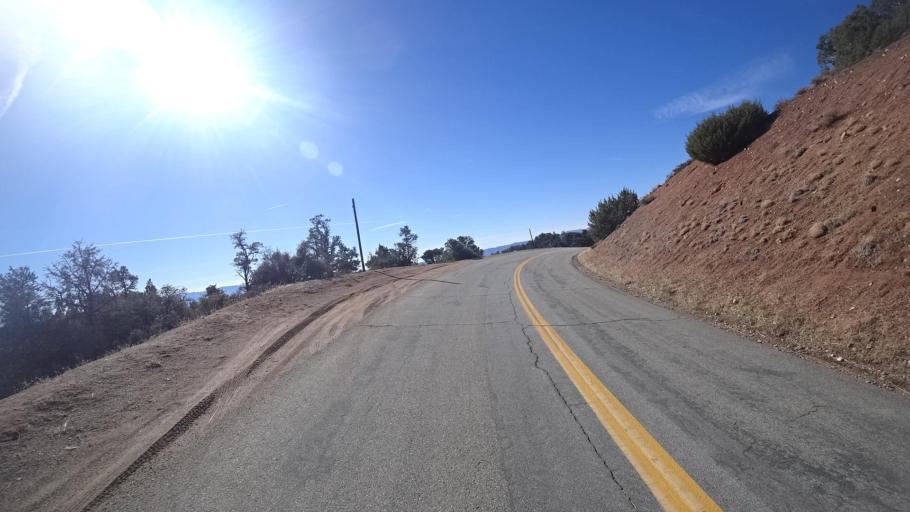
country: US
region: California
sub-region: Kern County
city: Pine Mountain Club
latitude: 34.8689
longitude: -119.3127
